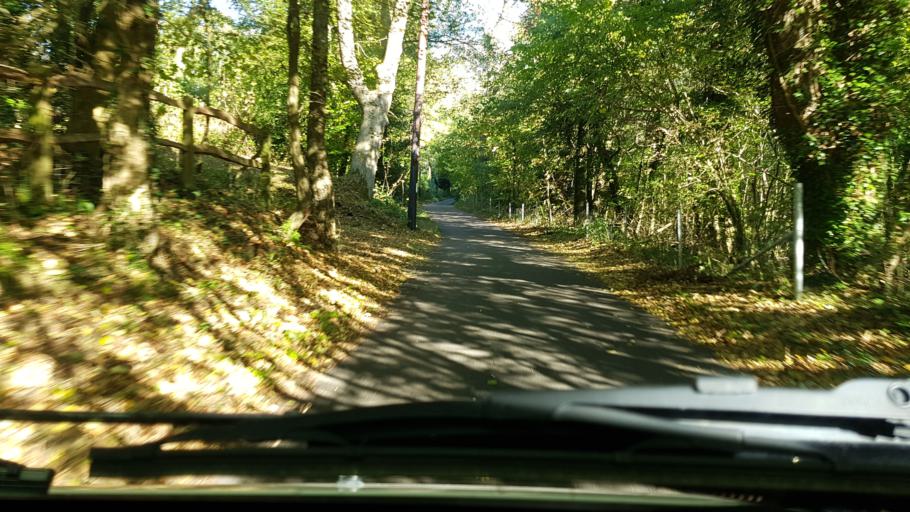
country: GB
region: England
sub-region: Surrey
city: Ockley
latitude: 51.1409
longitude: -0.3363
